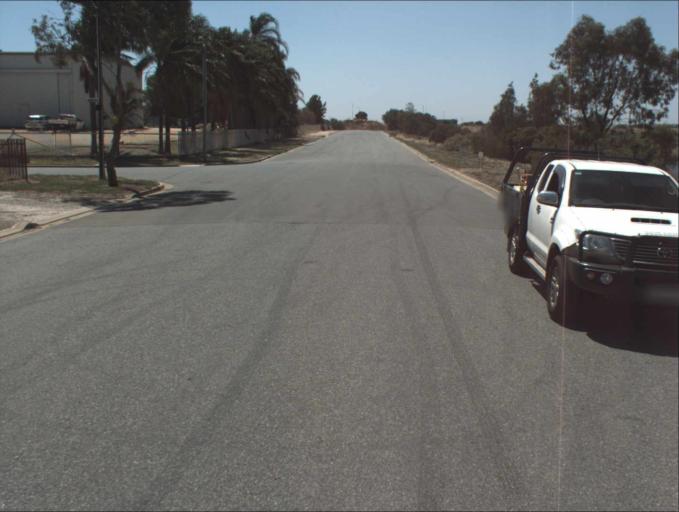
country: AU
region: South Australia
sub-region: Port Adelaide Enfield
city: Blair Athol
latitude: -34.8367
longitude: 138.5682
